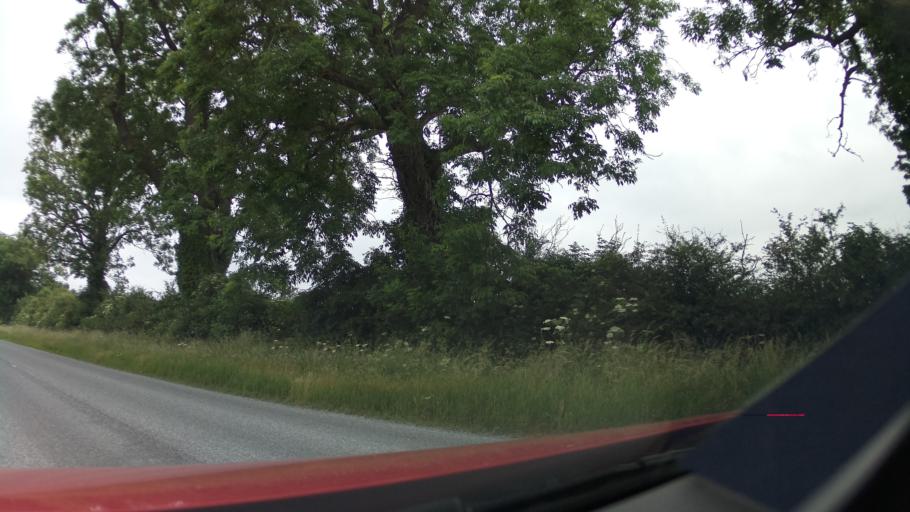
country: GB
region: England
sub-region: District of Rutland
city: Exton
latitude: 52.6732
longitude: -0.6548
